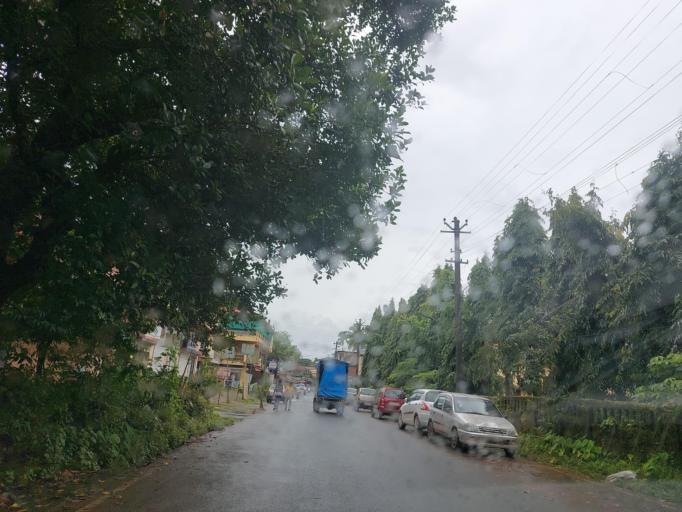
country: IN
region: Goa
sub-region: North Goa
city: Valpoy
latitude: 15.5332
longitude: 74.1370
